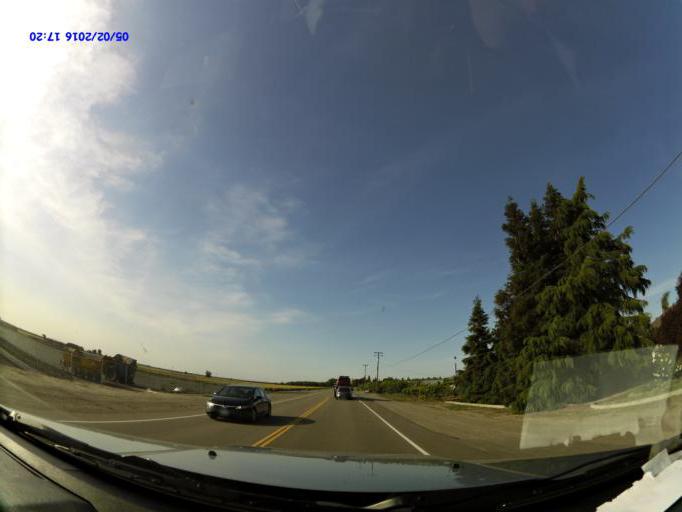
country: US
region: California
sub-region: San Joaquin County
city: Manteca
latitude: 37.8326
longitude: -121.1446
